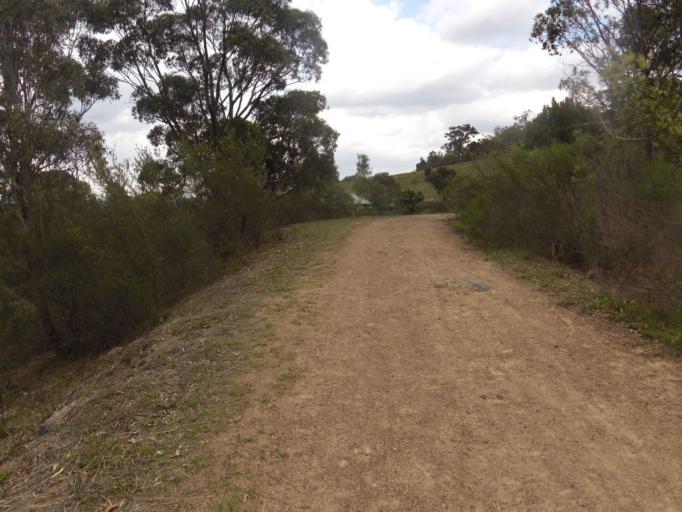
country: AU
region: Australian Capital Territory
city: Forrest
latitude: -35.3615
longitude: 149.1129
